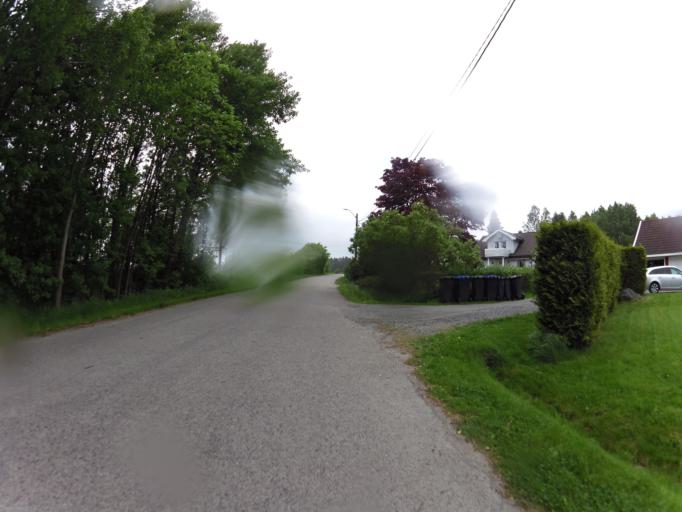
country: NO
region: Ostfold
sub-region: Rygge
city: Ryggebyen
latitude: 59.3661
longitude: 10.7755
